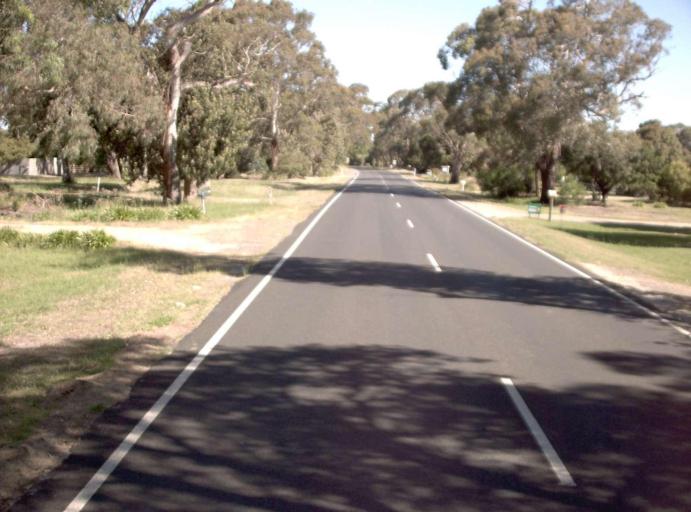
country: AU
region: Victoria
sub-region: Latrobe
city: Traralgon
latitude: -38.6513
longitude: 146.6754
